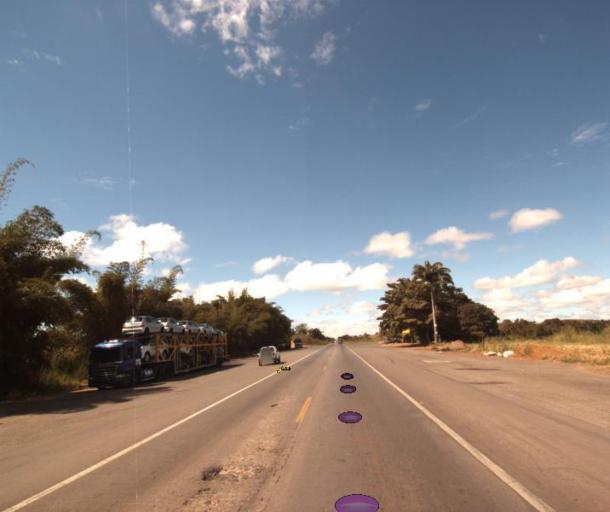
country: BR
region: Goias
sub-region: Rialma
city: Rialma
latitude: -15.4806
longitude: -49.4937
